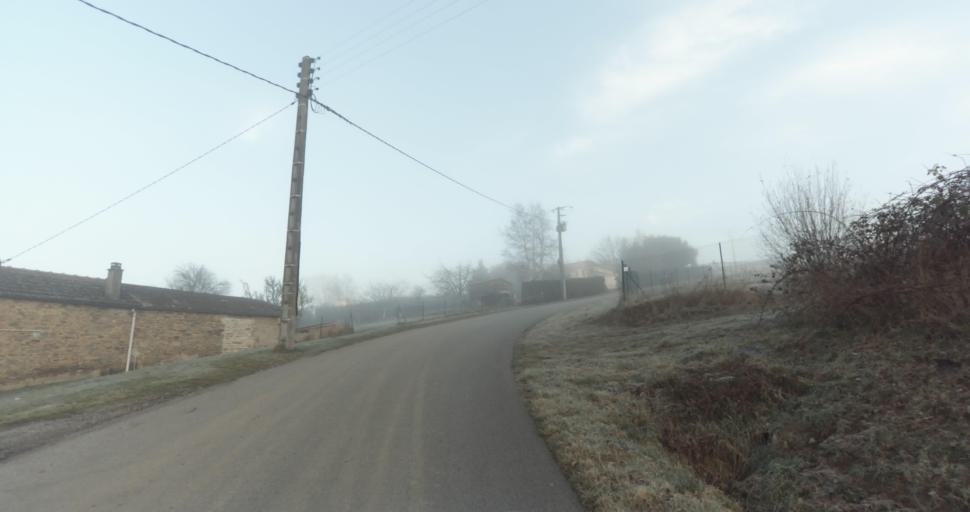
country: FR
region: Limousin
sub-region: Departement de la Haute-Vienne
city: Aixe-sur-Vienne
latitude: 45.7913
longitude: 1.1610
